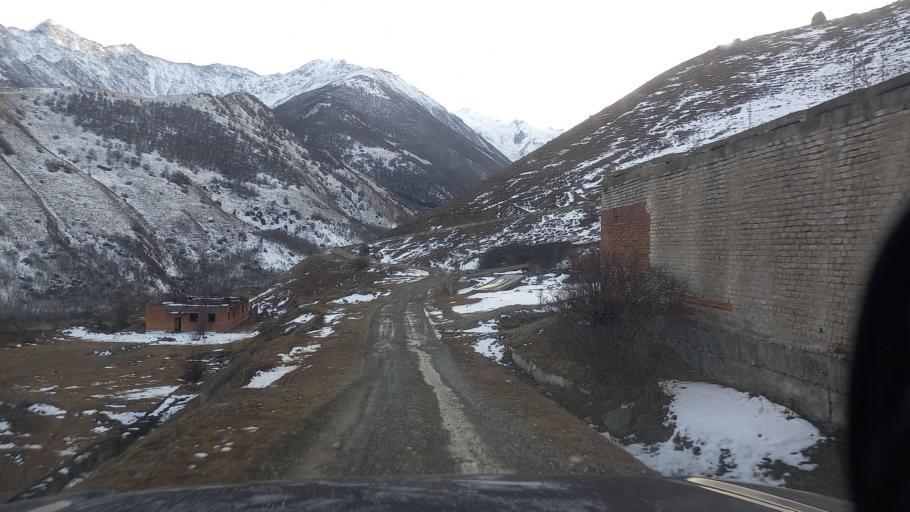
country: RU
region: Ingushetiya
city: Dzhayrakh
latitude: 42.8432
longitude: 44.5125
